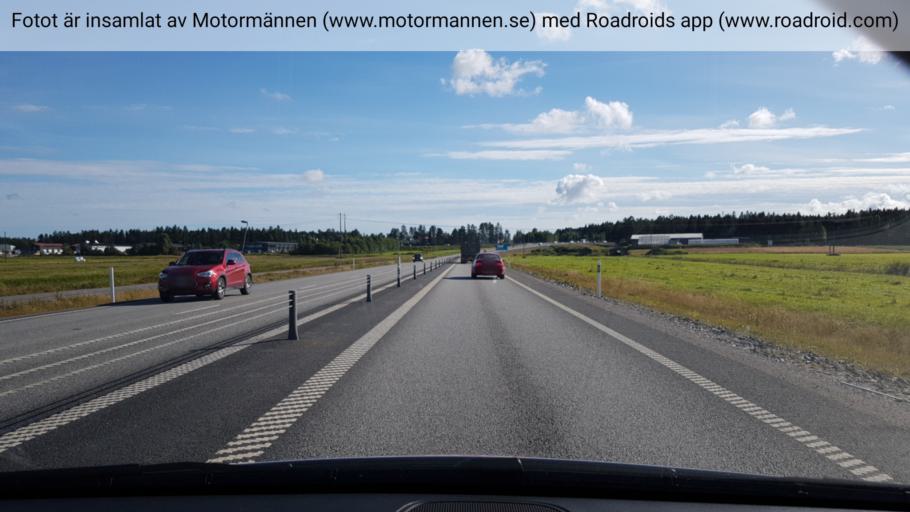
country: SE
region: Vaesterbotten
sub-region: Umea Kommun
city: Roback
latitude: 63.8479
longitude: 20.1906
